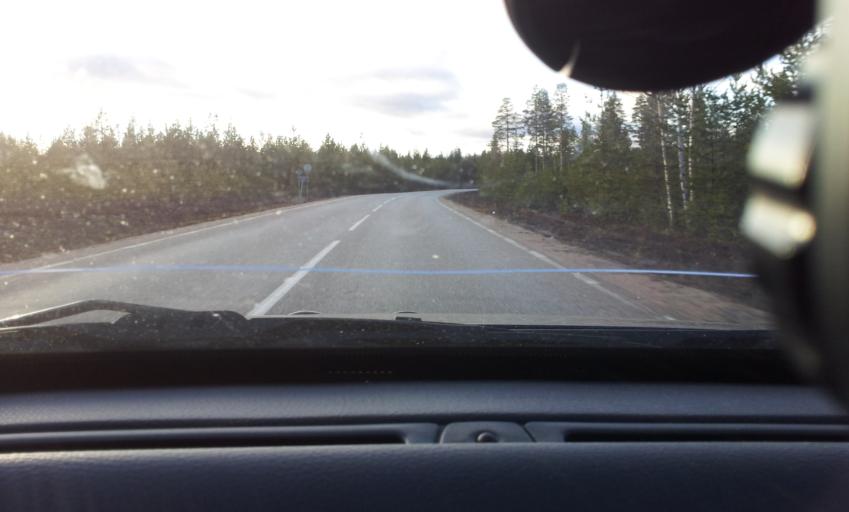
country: SE
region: Jaemtland
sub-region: Harjedalens Kommun
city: Sveg
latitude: 62.1158
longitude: 15.0471
